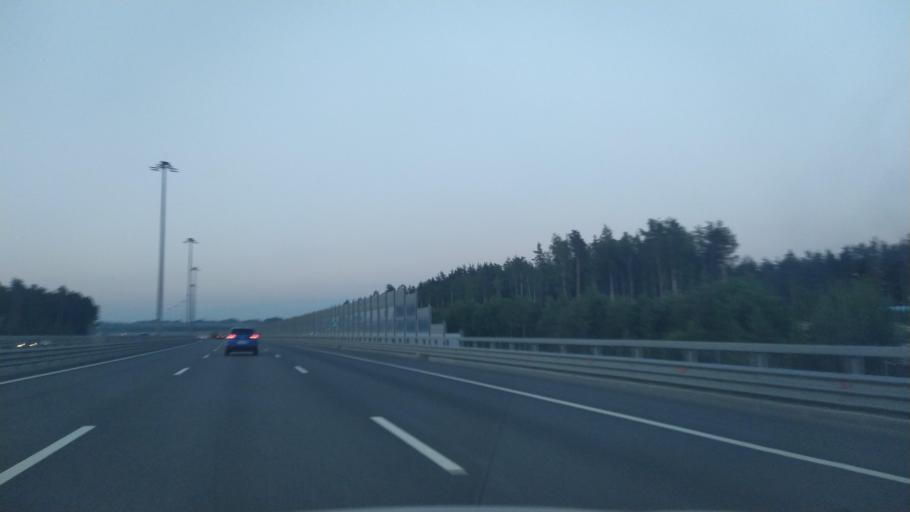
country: RU
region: St.-Petersburg
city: Levashovo
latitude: 60.0839
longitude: 30.2156
